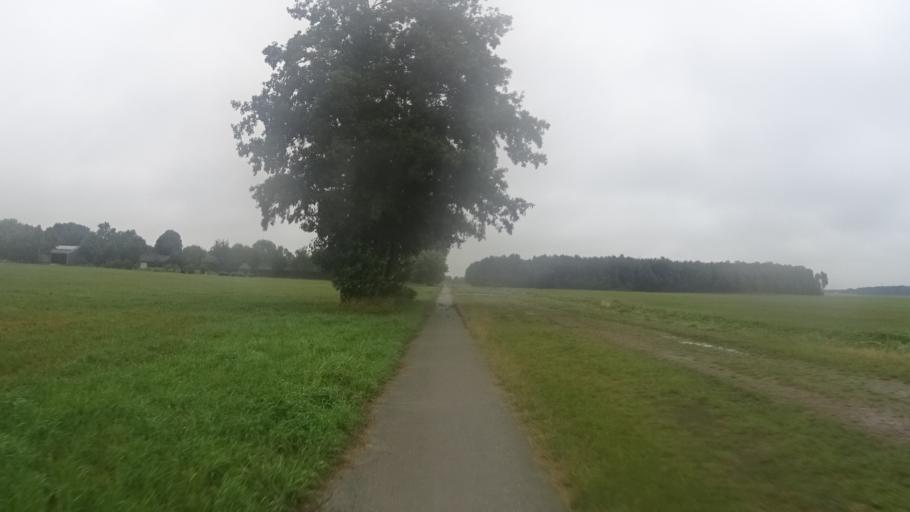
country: NL
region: Groningen
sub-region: Gemeente Veendam
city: Veendam
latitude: 53.1842
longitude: 6.8787
